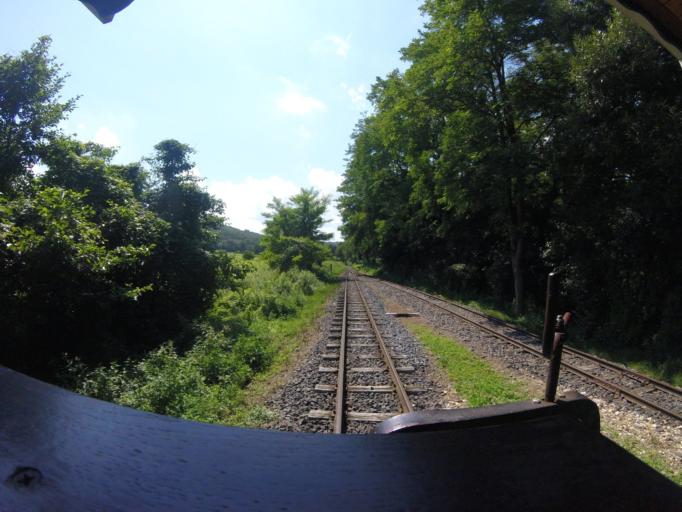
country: HU
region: Zala
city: Letenye
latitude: 46.5689
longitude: 16.6776
